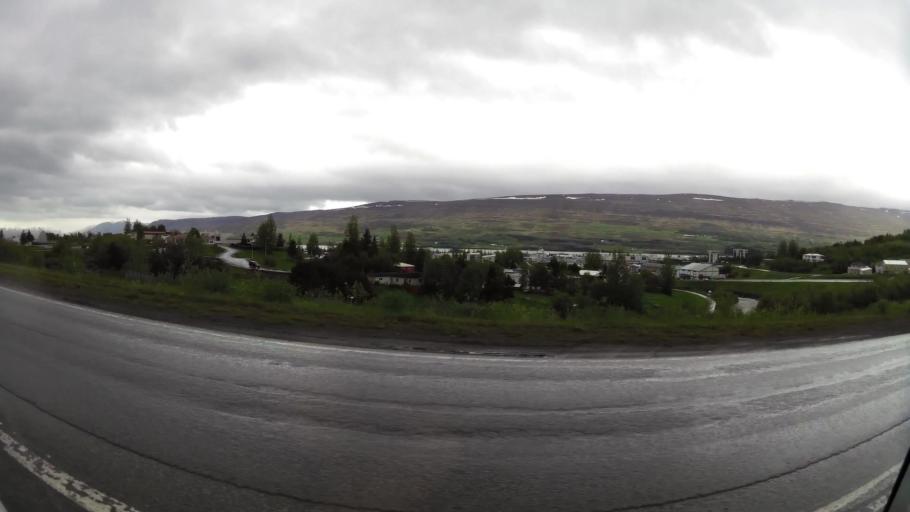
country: IS
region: Northeast
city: Akureyri
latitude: 65.6865
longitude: -18.1161
